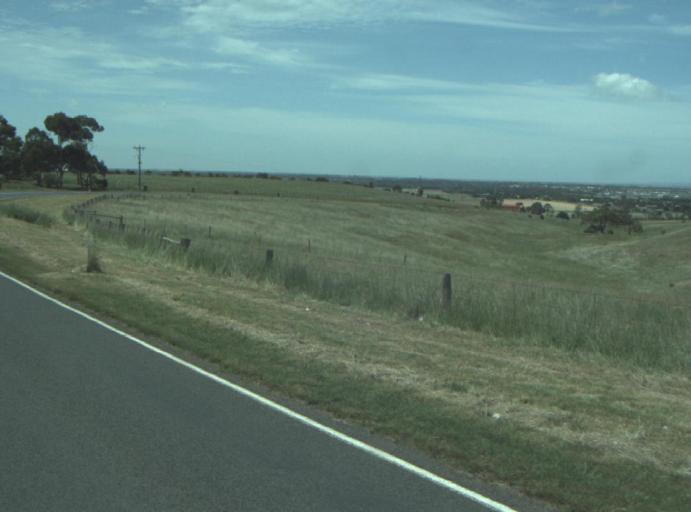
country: AU
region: Victoria
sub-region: Greater Geelong
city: Lara
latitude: -38.0119
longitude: 144.3338
